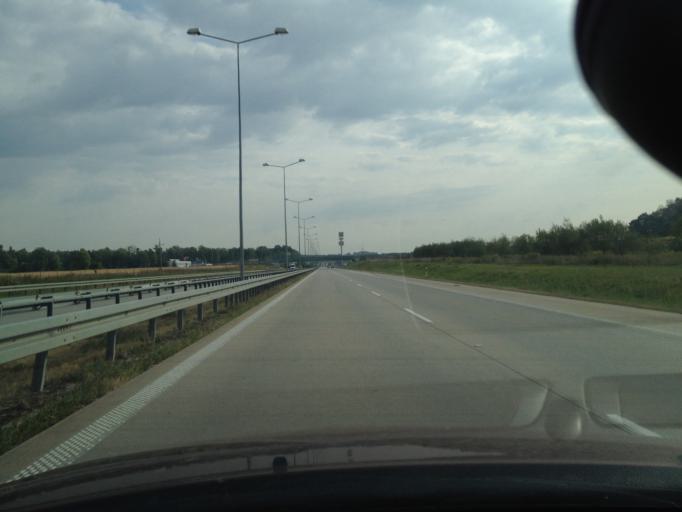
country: PL
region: Lower Silesian Voivodeship
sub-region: Powiat zgorzelecki
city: Lagow
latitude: 51.1845
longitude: 15.1000
